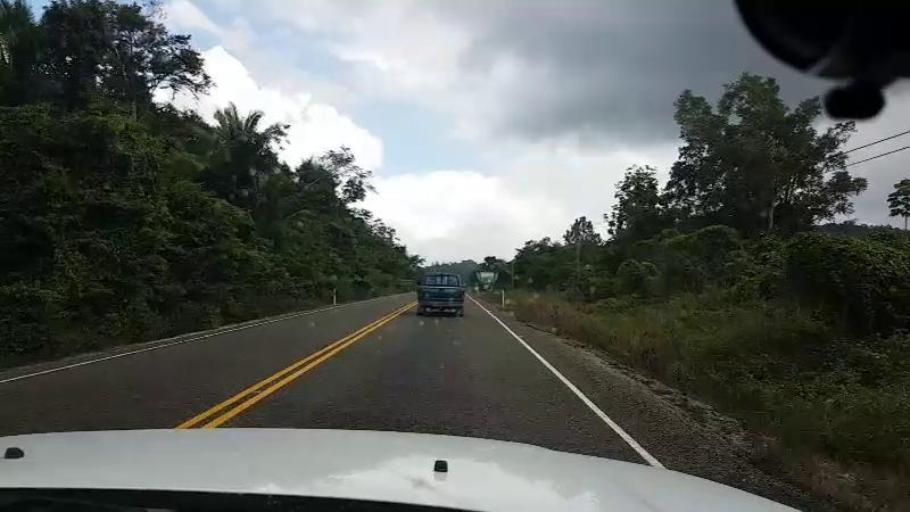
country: BZ
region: Cayo
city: Belmopan
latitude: 17.1532
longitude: -88.6725
